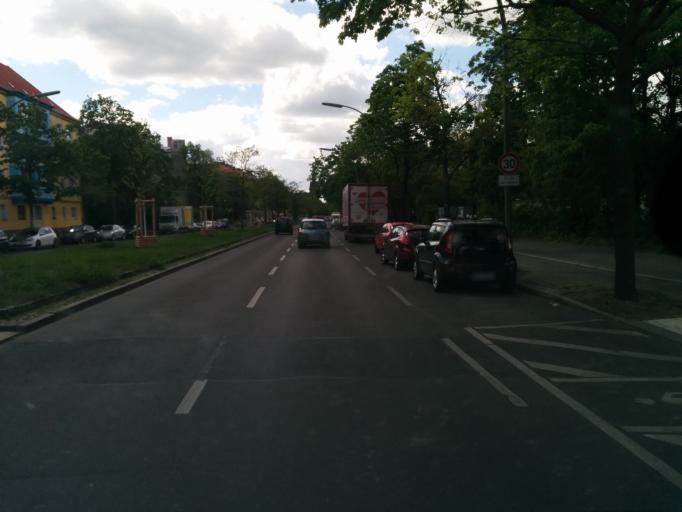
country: DE
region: Berlin
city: Wilhelmstadt
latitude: 52.5243
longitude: 13.1925
